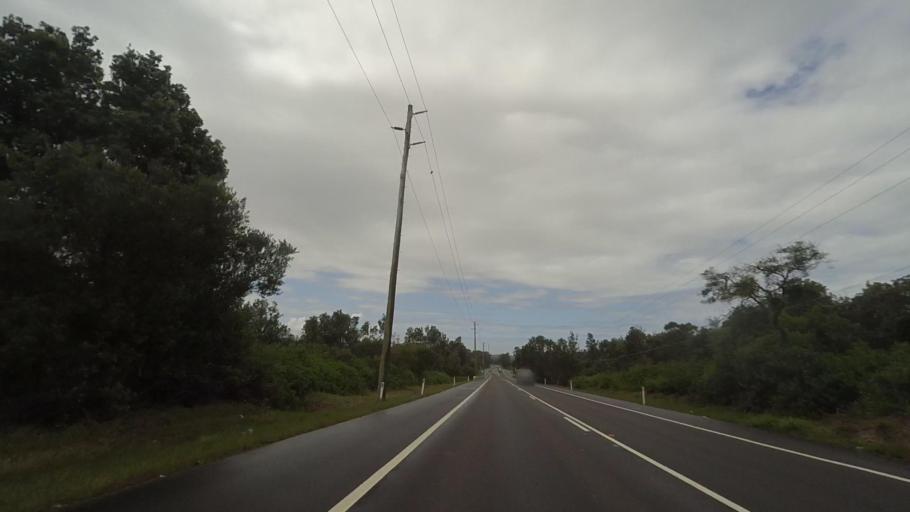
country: AU
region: New South Wales
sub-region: Wyong Shire
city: The Entrance
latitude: -33.3221
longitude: 151.5144
